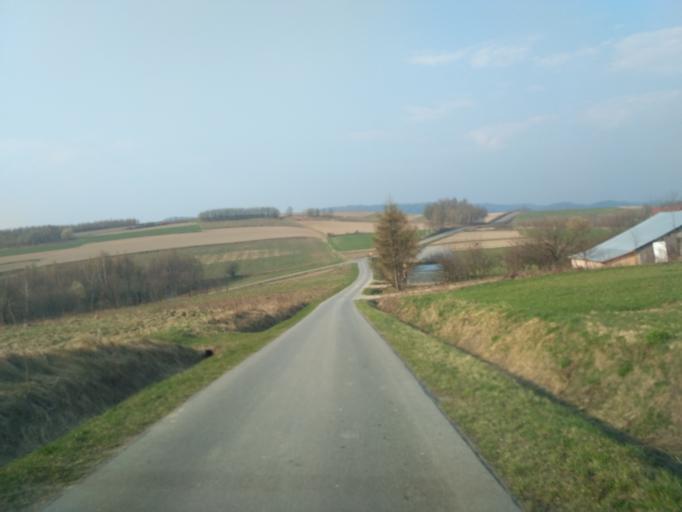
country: PL
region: Subcarpathian Voivodeship
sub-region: Powiat ropczycko-sedziszowski
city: Wielopole Skrzynskie
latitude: 49.9026
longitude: 21.5862
